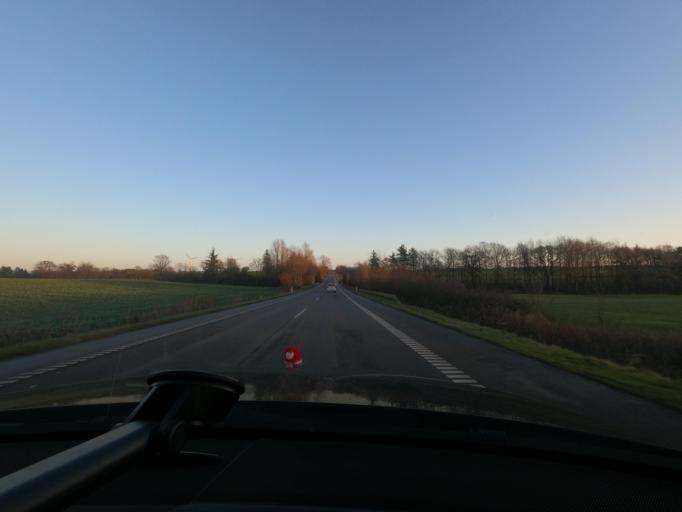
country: DK
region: South Denmark
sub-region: Sonderborg Kommune
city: Horuphav
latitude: 54.9087
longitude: 9.9240
